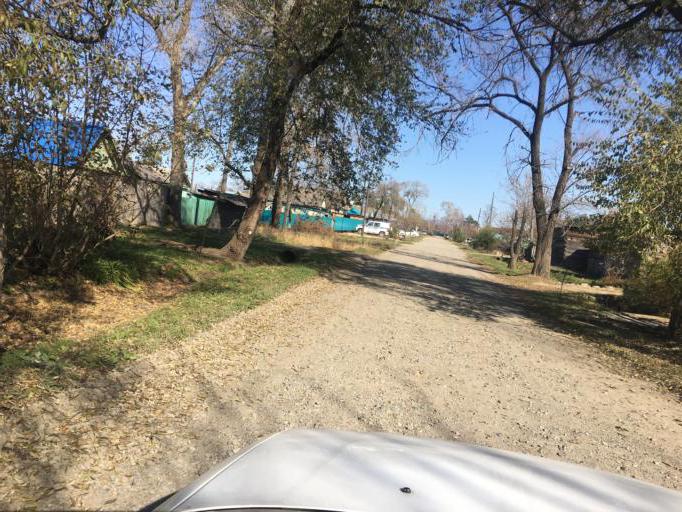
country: RU
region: Primorskiy
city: Dal'nerechensk
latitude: 45.9267
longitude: 133.7496
